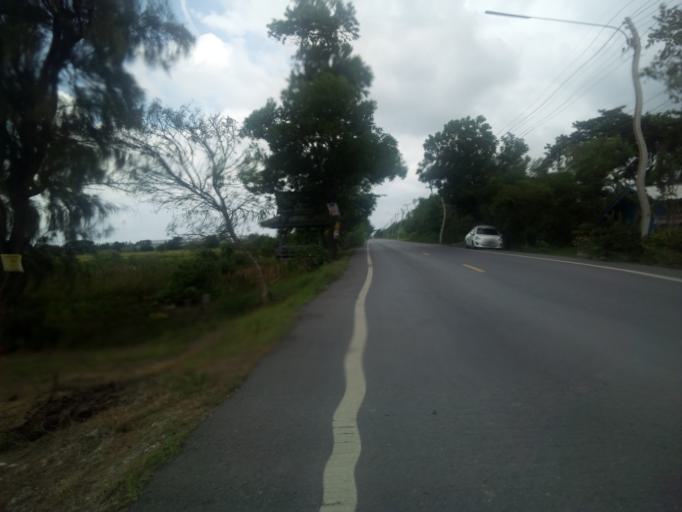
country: TH
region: Pathum Thani
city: Ban Lam Luk Ka
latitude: 14.0215
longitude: 100.8237
